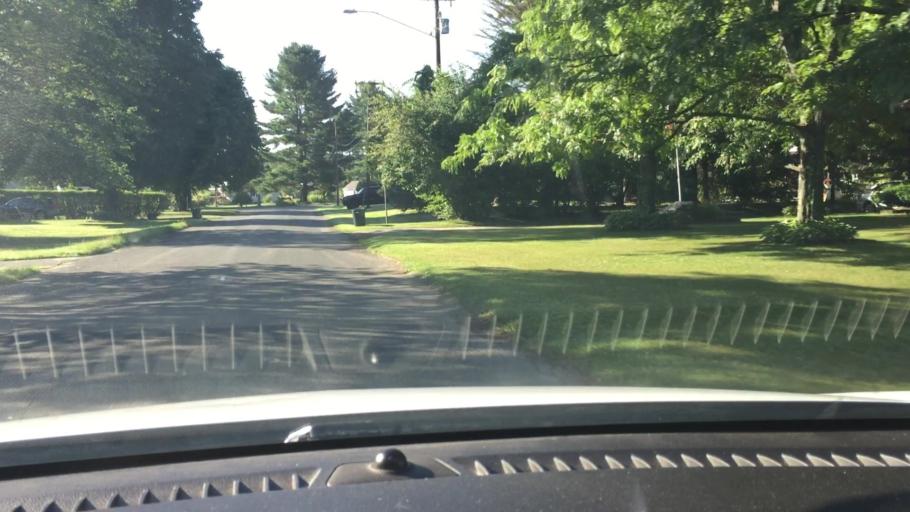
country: US
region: Massachusetts
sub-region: Berkshire County
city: Pittsfield
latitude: 42.4492
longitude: -73.2184
